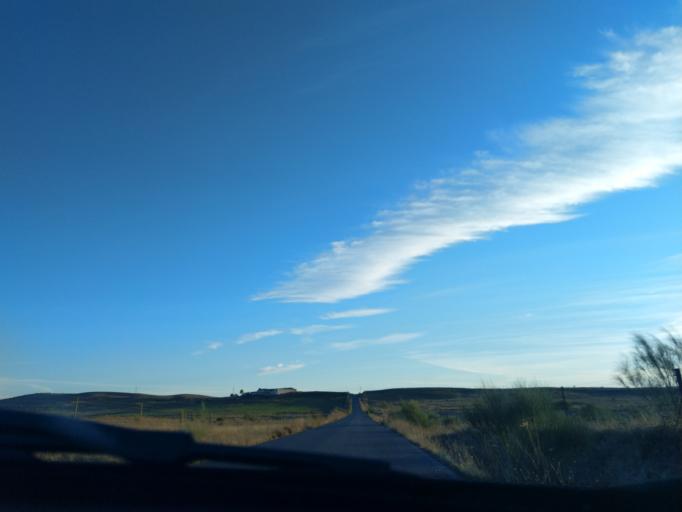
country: ES
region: Extremadura
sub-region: Provincia de Badajoz
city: Berlanga
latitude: 38.2664
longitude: -5.8239
